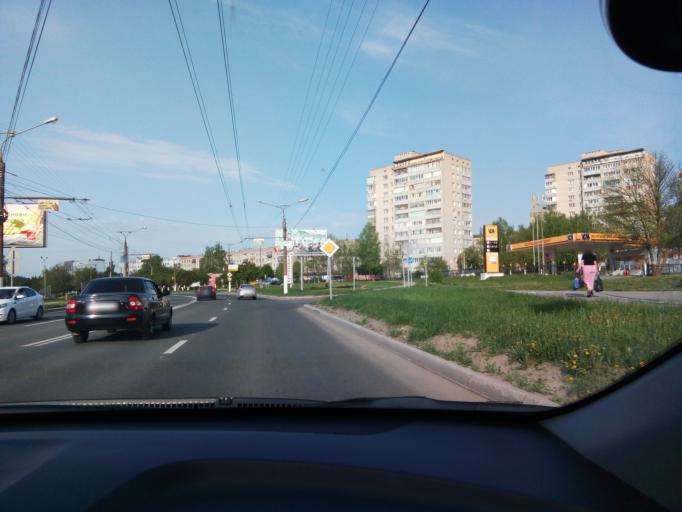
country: RU
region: Chuvashia
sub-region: Cheboksarskiy Rayon
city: Cheboksary
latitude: 56.1267
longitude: 47.2658
